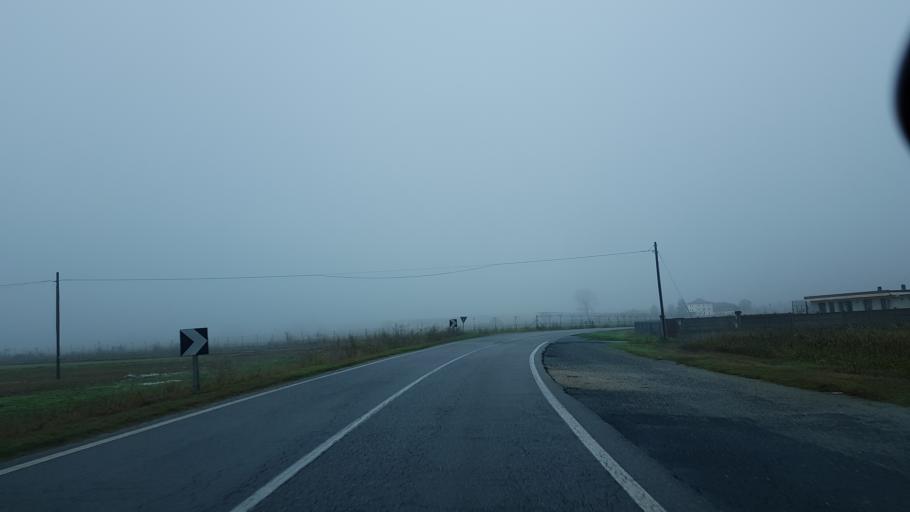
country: IT
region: Piedmont
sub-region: Provincia di Cuneo
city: Genola
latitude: 44.5567
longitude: 7.6358
